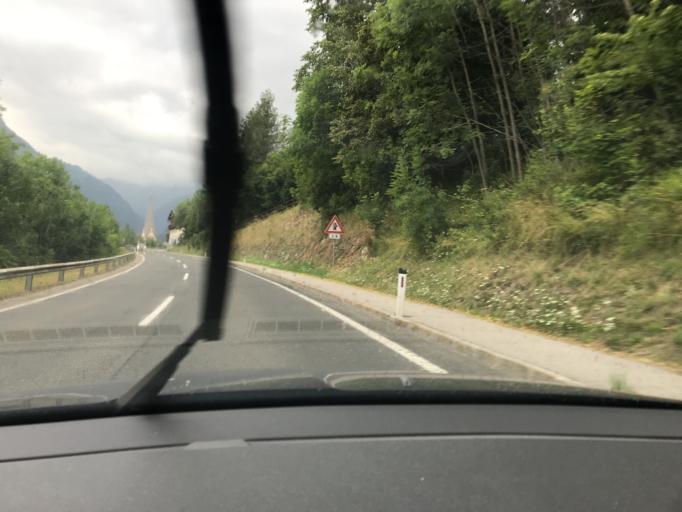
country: AT
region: Tyrol
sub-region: Politischer Bezirk Lienz
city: Matrei in Osttirol
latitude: 46.9967
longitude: 12.5444
